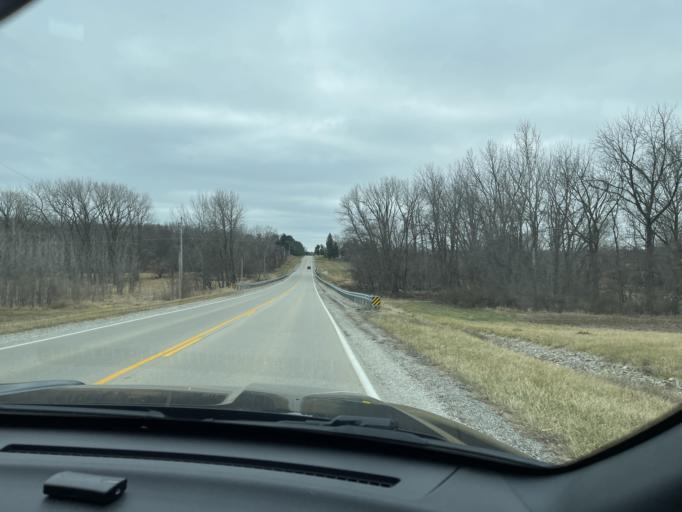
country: US
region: Illinois
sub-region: Sangamon County
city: Leland Grove
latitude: 39.8121
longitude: -89.7395
